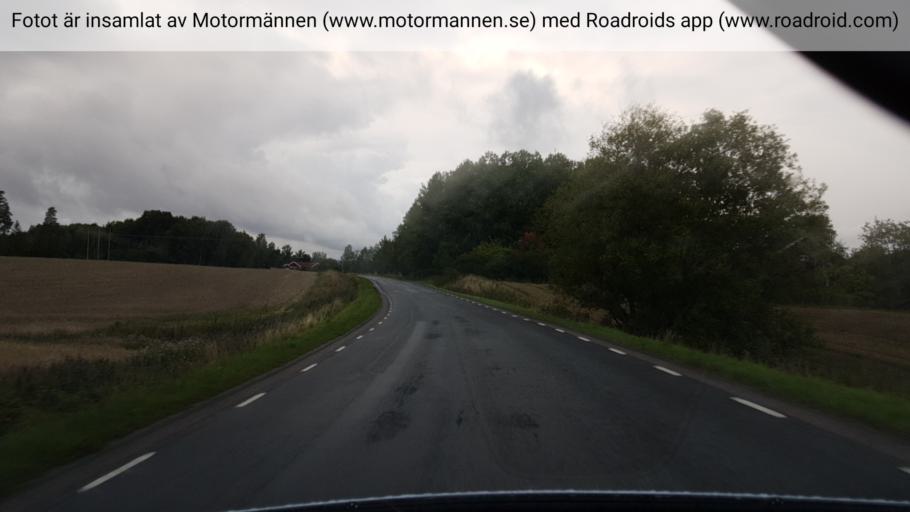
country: SE
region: Vaestra Goetaland
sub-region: Skovde Kommun
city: Skoevde
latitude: 58.3783
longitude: 13.9266
